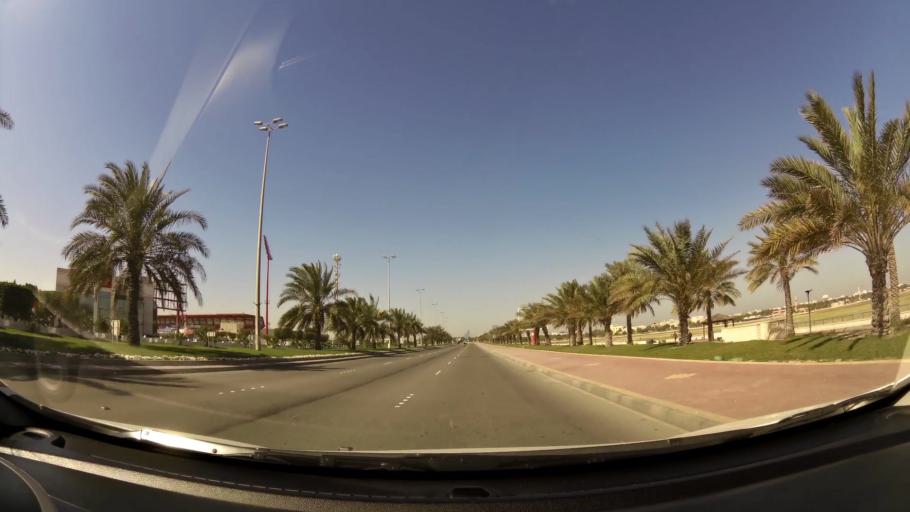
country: BH
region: Muharraq
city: Al Muharraq
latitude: 26.2598
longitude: 50.6285
